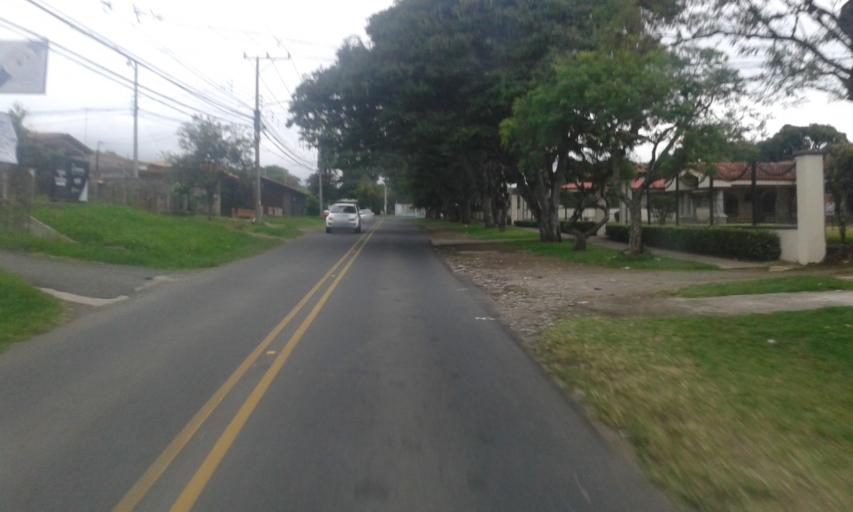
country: CR
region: San Jose
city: San Juan
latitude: 9.9781
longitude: -84.0830
